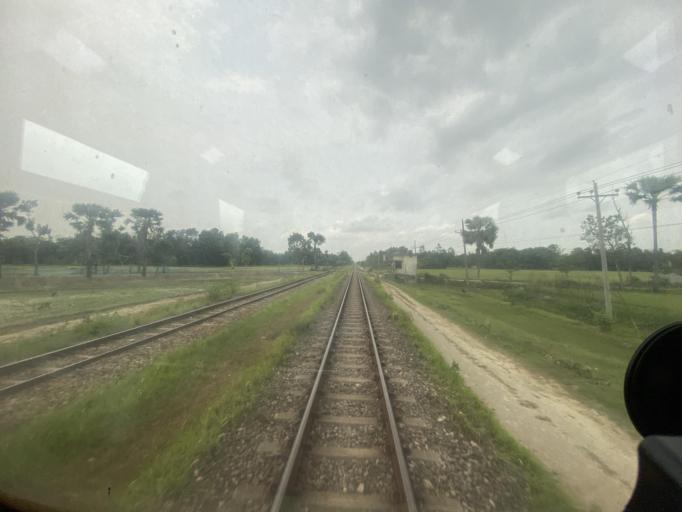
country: BD
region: Chittagong
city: Laksham
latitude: 23.1935
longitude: 91.1681
